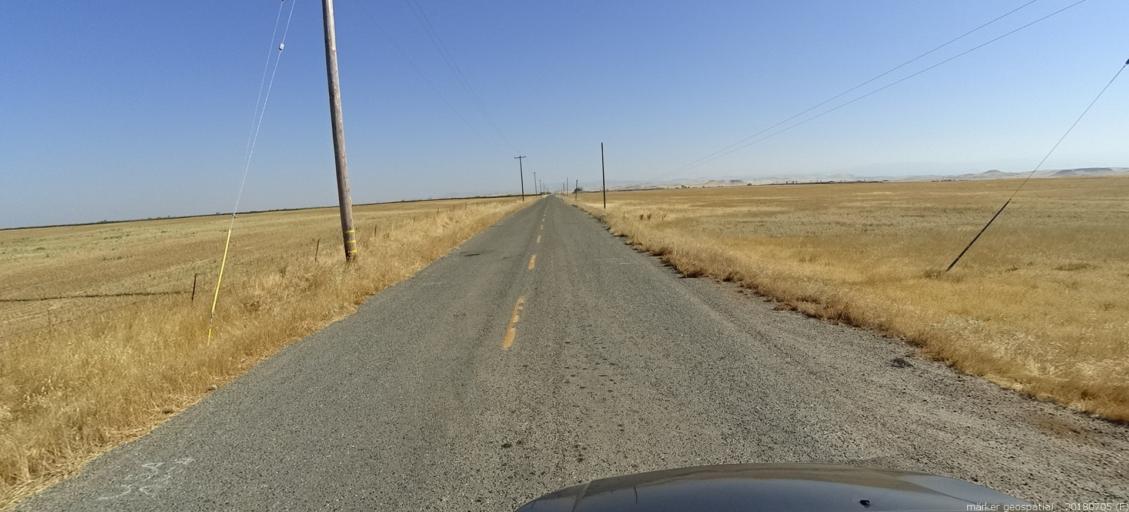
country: US
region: California
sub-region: Madera County
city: Madera Acres
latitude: 37.1413
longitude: -120.0747
